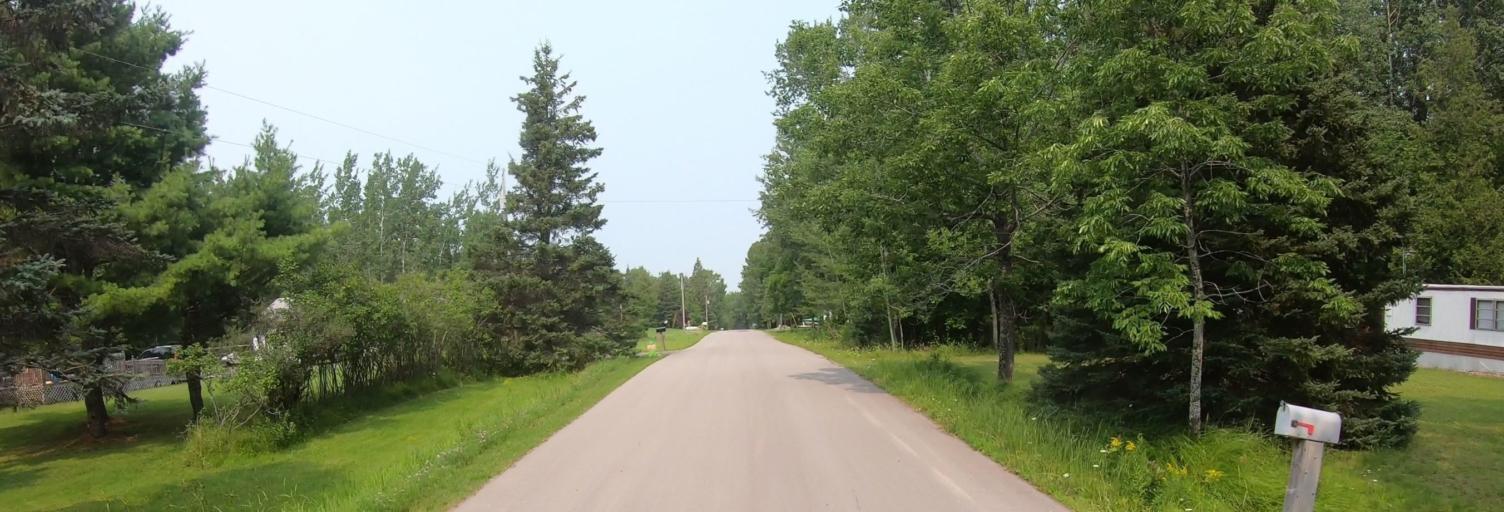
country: CA
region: Ontario
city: Thessalon
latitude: 46.0315
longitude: -83.6788
